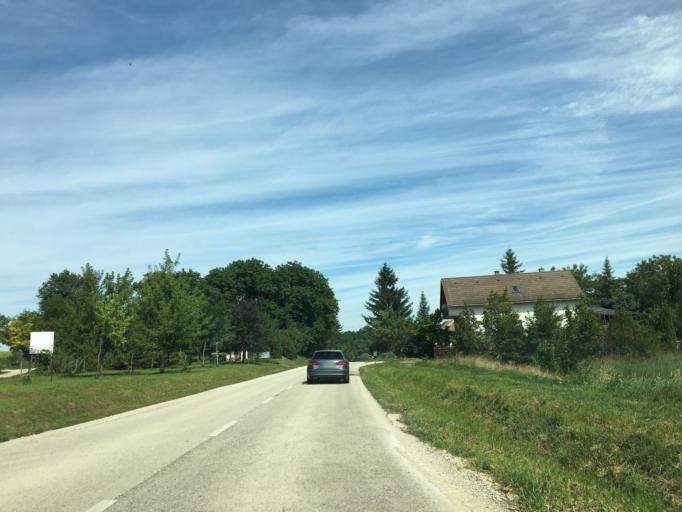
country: HU
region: Komarom-Esztergom
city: Bajna
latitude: 47.6436
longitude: 18.6054
